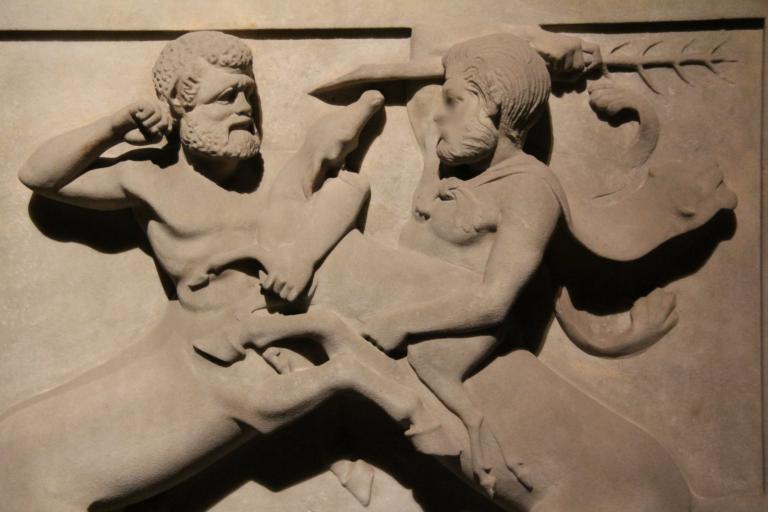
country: TR
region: Istanbul
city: Eminoenue
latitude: 41.0116
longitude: 28.9815
